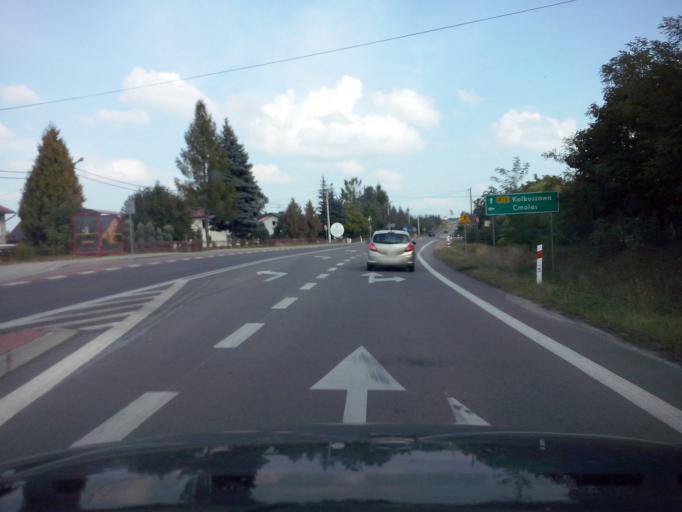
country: PL
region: Subcarpathian Voivodeship
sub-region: Powiat kolbuszowski
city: Niwiska
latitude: 50.2759
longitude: 21.6052
